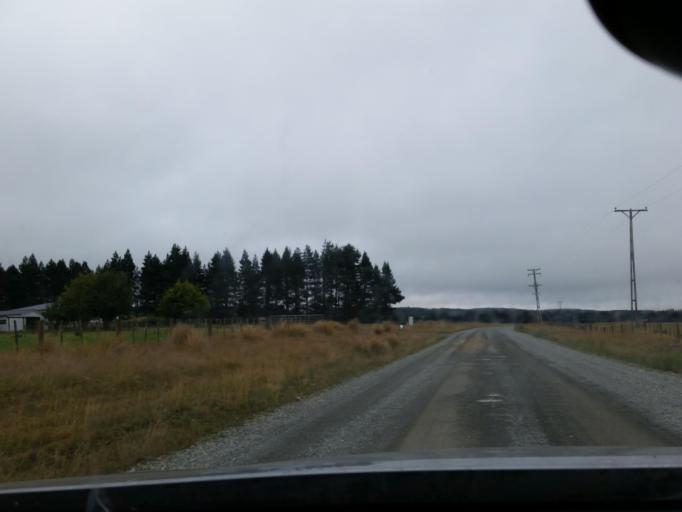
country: NZ
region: Southland
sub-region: Southland District
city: Te Anau
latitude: -45.5504
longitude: 168.1209
